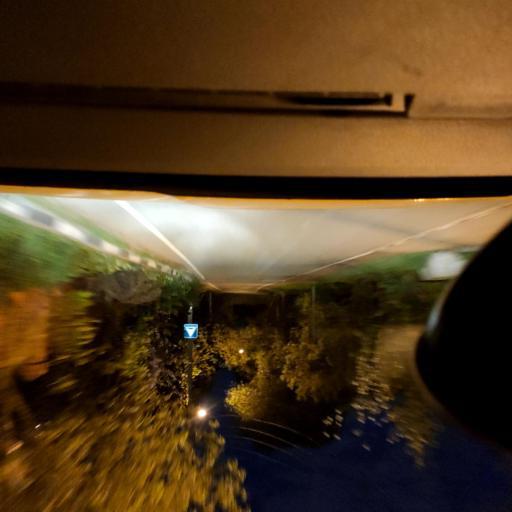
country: RU
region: Moscow
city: Zagor'ye
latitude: 55.5304
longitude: 37.6483
